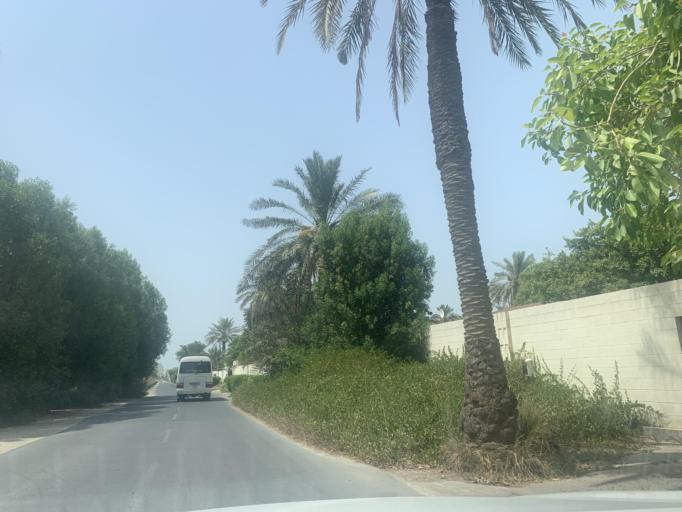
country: BH
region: Manama
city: Jidd Hafs
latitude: 26.2255
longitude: 50.4664
